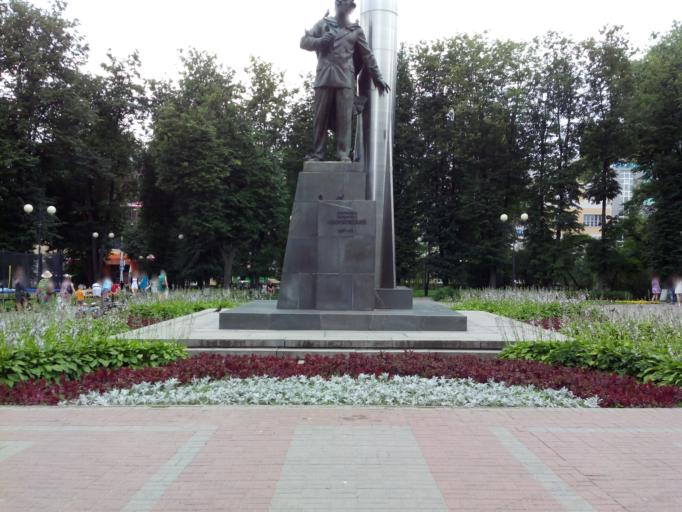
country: RU
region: Kaluga
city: Kaluga
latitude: 54.5157
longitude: 36.2446
